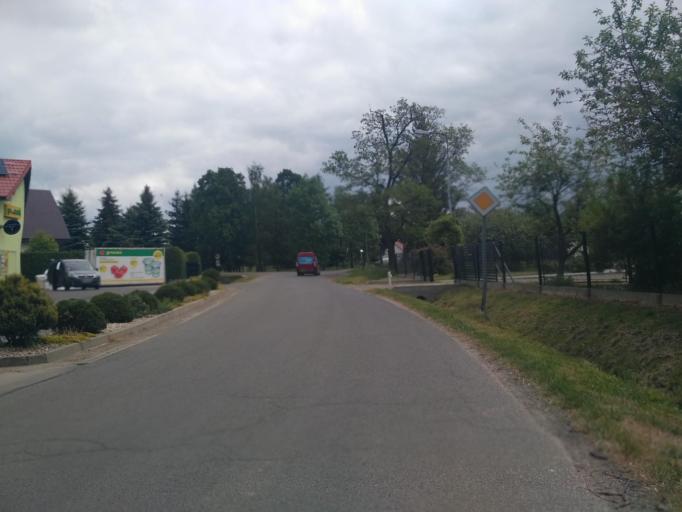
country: PL
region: Subcarpathian Voivodeship
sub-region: Powiat krosnienski
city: Jedlicze
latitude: 49.7051
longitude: 21.6381
